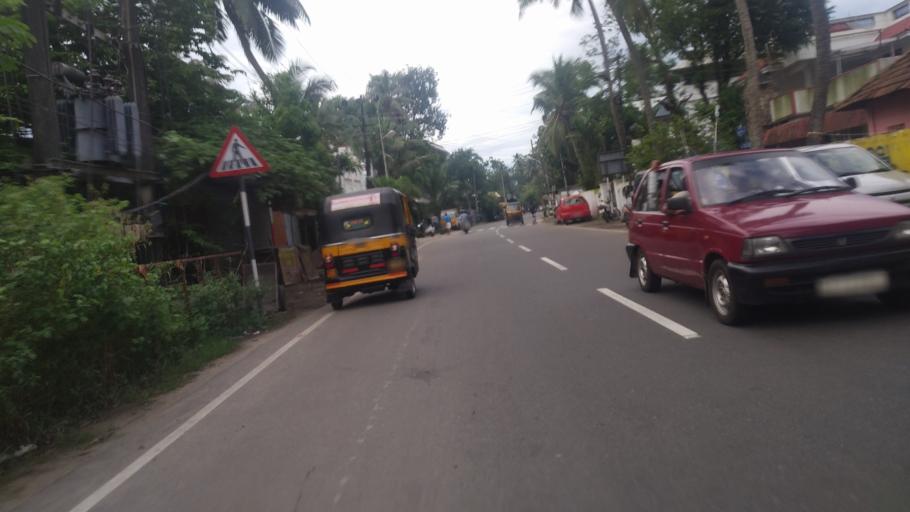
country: IN
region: Kerala
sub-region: Ernakulam
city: Cochin
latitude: 9.9360
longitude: 76.2456
